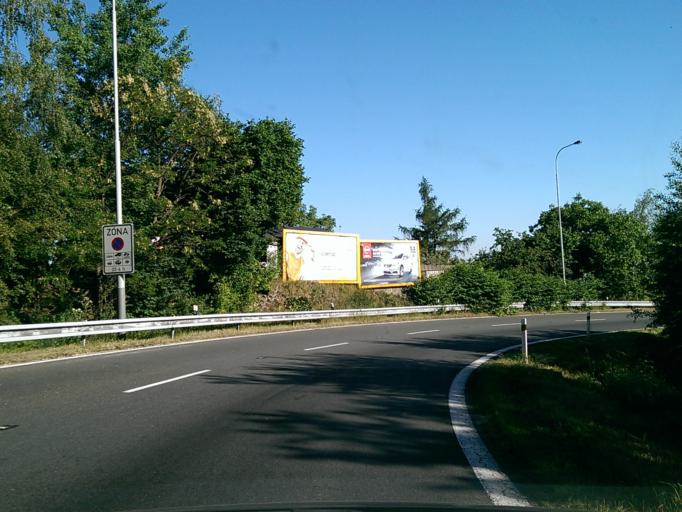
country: CZ
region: Praha
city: Cerny Most
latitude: 50.1120
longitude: 14.5892
